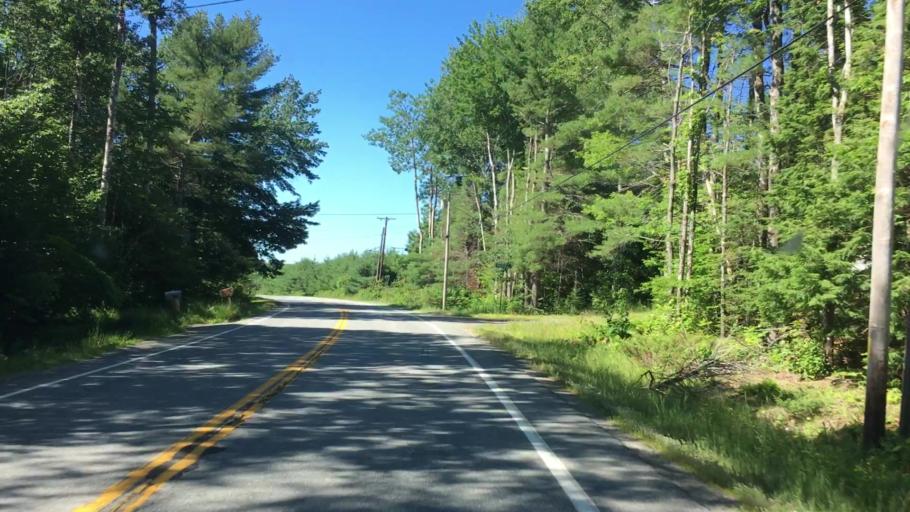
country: US
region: Maine
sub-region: Hancock County
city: Dedham
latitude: 44.6748
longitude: -68.6713
